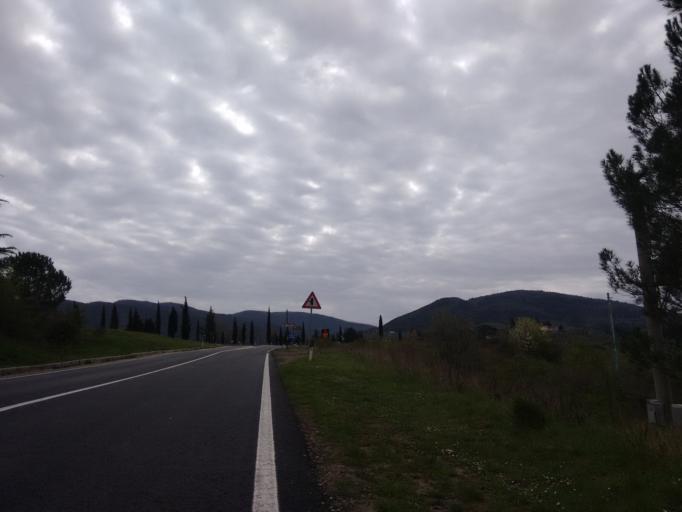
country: IT
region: Tuscany
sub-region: Province of Florence
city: Strada in Chianti
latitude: 43.6527
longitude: 11.3065
